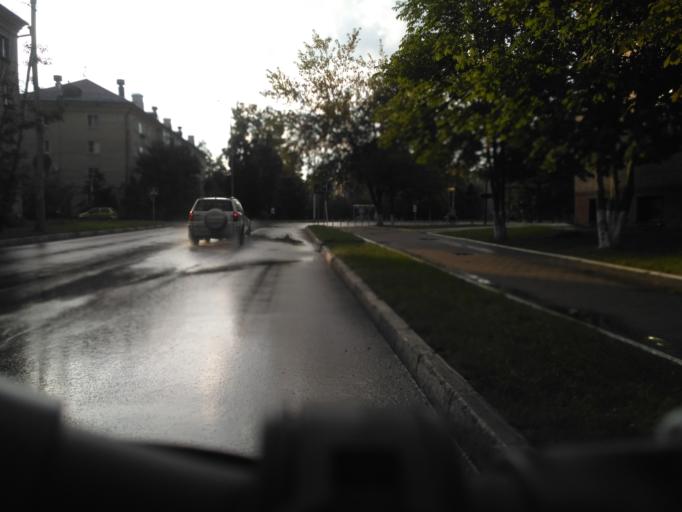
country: RU
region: Moskovskaya
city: Dubna
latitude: 56.7506
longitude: 37.2034
